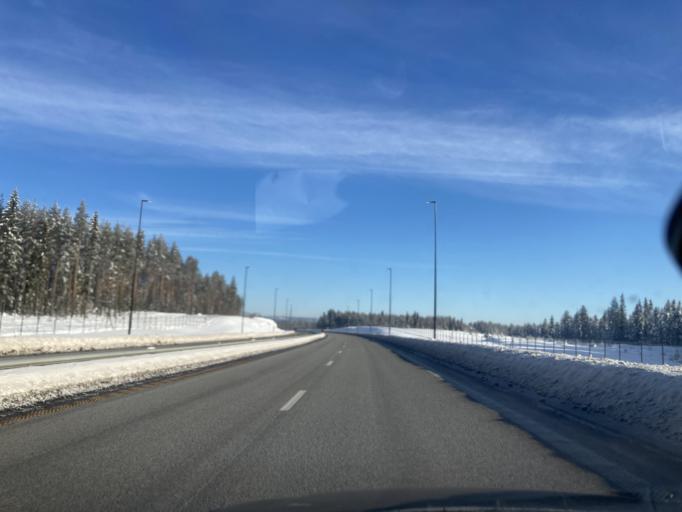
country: NO
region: Hedmark
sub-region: Loten
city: Loten
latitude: 60.8659
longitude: 11.4317
